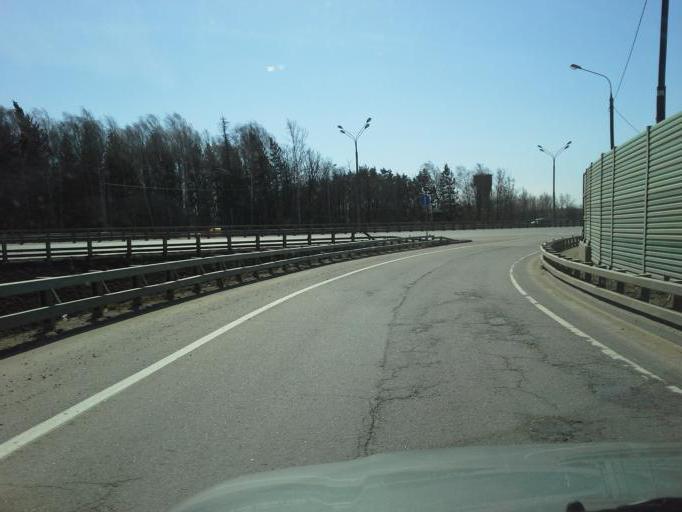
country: RU
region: Moskovskaya
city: Kokoshkino
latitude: 55.6239
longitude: 37.1499
